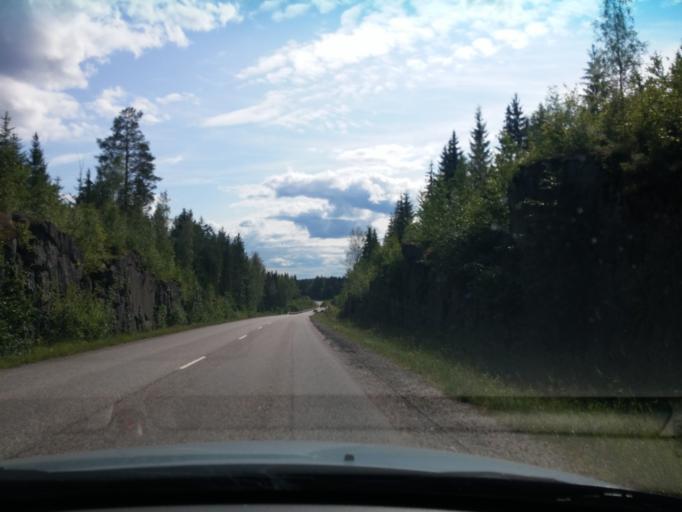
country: FI
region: Central Finland
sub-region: Keuruu
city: Keuruu
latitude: 62.2838
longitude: 24.6952
